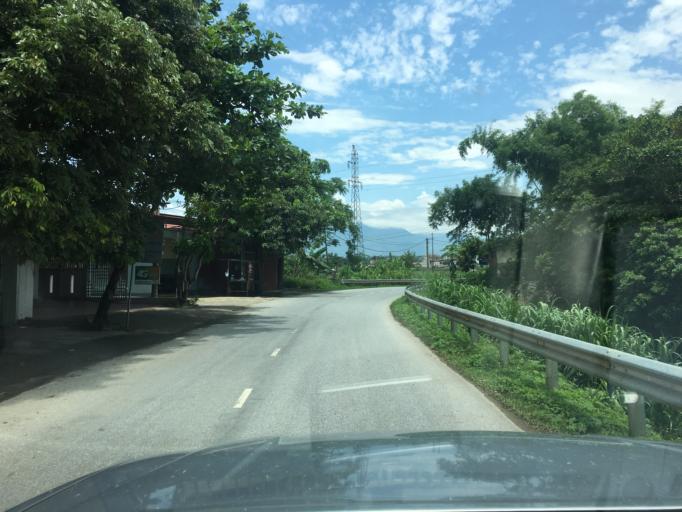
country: VN
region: Yen Bai
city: Son Thinh
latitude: 21.6470
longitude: 104.5011
